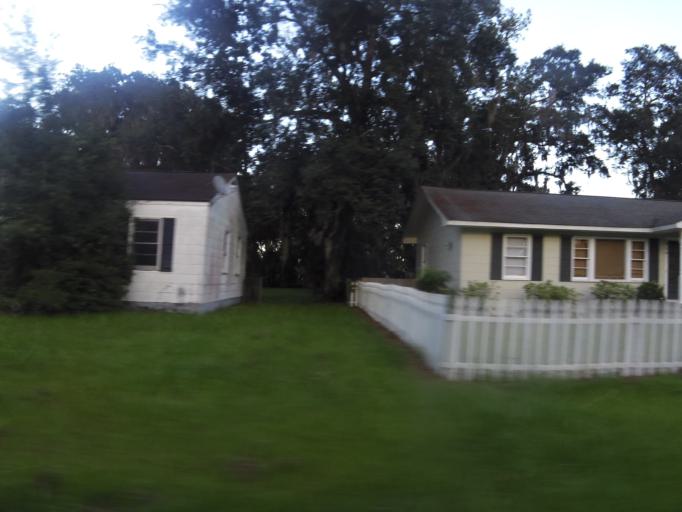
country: US
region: Georgia
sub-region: Camden County
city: St. Marys
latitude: 30.7345
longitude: -81.5558
